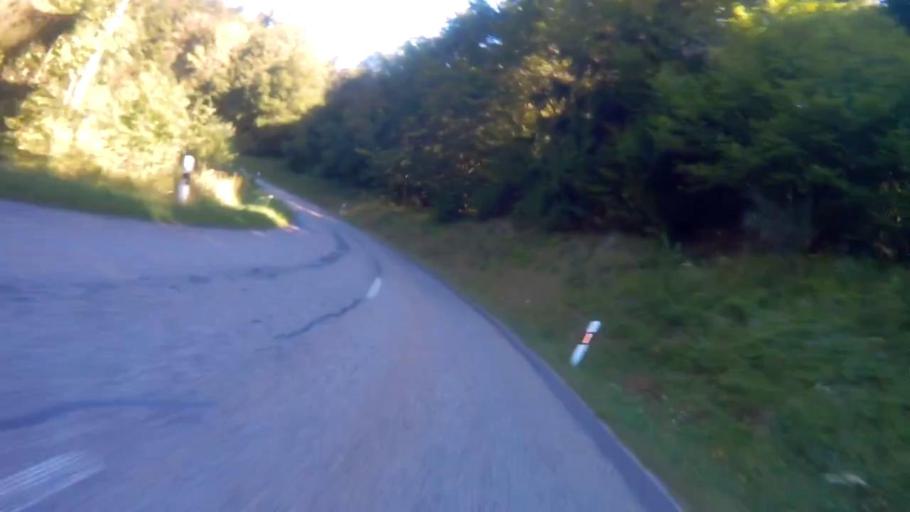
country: DE
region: Baden-Wuerttemberg
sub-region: Freiburg Region
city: Sulzburg
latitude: 47.7730
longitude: 7.7446
